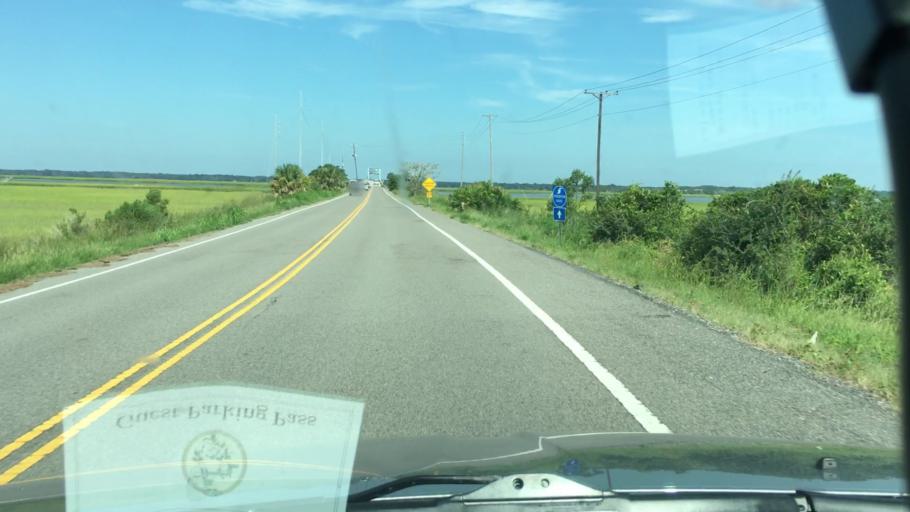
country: US
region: South Carolina
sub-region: Beaufort County
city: Beaufort
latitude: 32.4022
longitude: -80.4469
